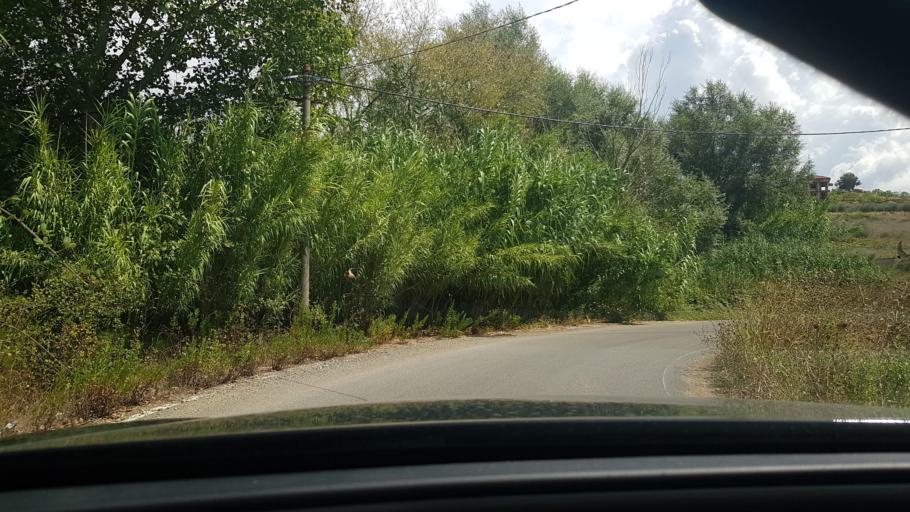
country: AL
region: Durres
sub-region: Rrethi i Durresit
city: Rrashbull
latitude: 41.2981
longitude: 19.5245
